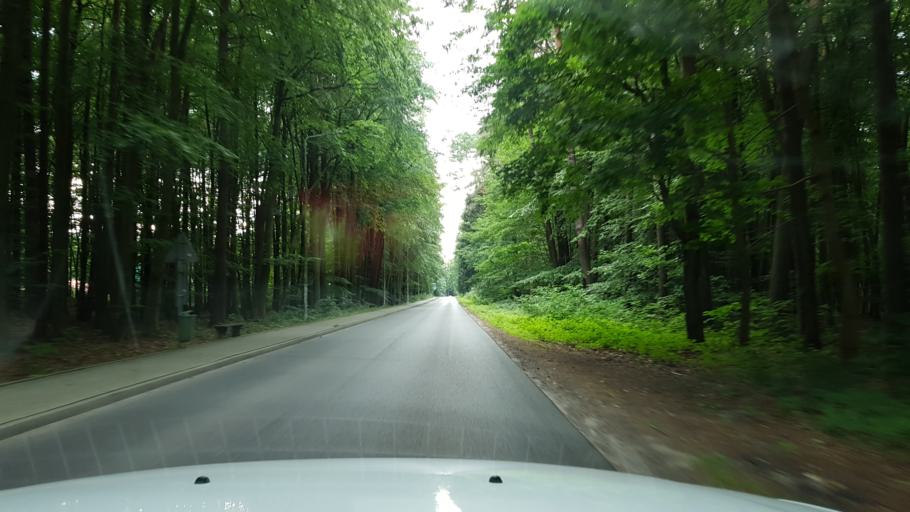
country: PL
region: West Pomeranian Voivodeship
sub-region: Powiat drawski
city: Zlocieniec
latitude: 53.5462
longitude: 16.0105
